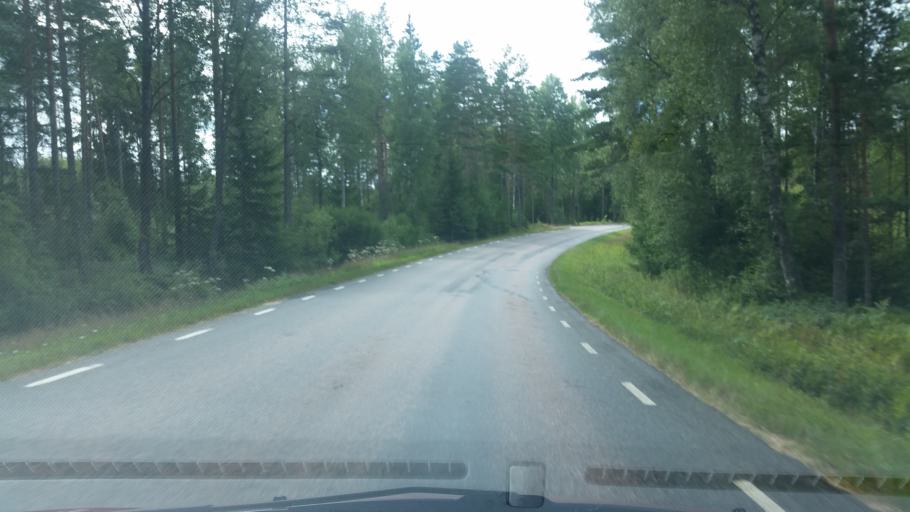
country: SE
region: Joenkoeping
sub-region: Gislaveds Kommun
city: Reftele
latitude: 57.2144
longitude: 13.6222
